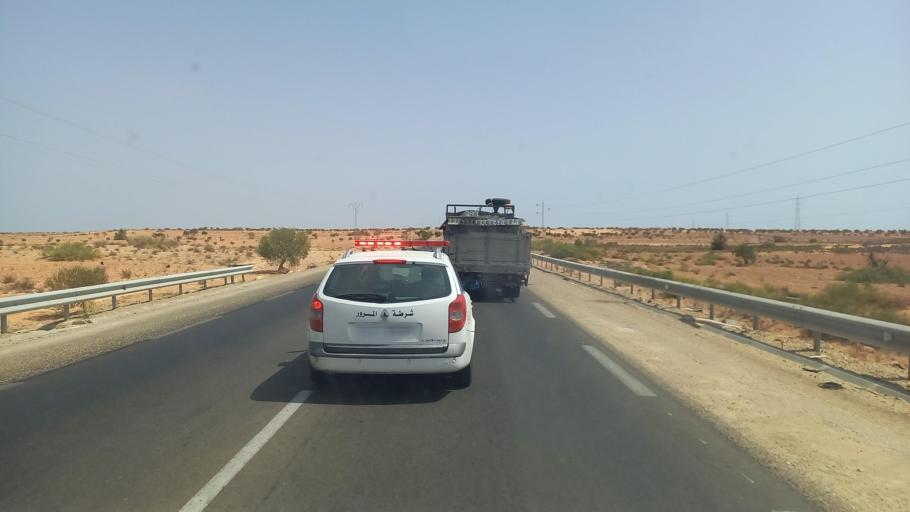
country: TN
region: Madanin
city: Zarzis
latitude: 33.4110
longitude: 10.8654
